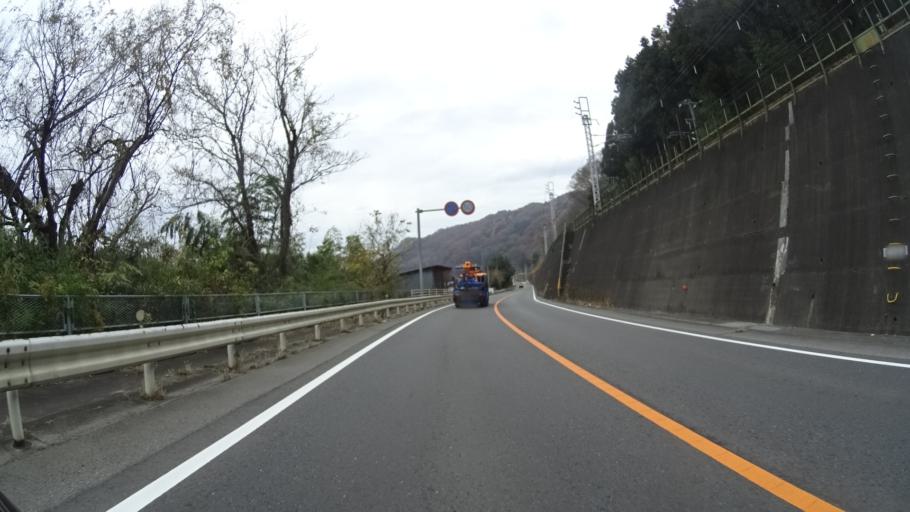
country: JP
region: Gunma
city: Numata
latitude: 36.6159
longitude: 139.0421
